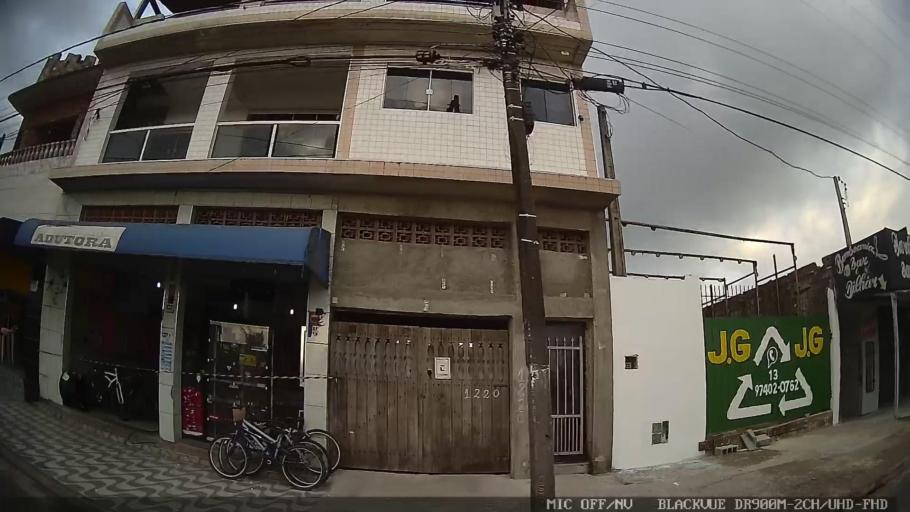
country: BR
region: Sao Paulo
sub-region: Itanhaem
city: Itanhaem
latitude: -24.1704
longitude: -46.7855
